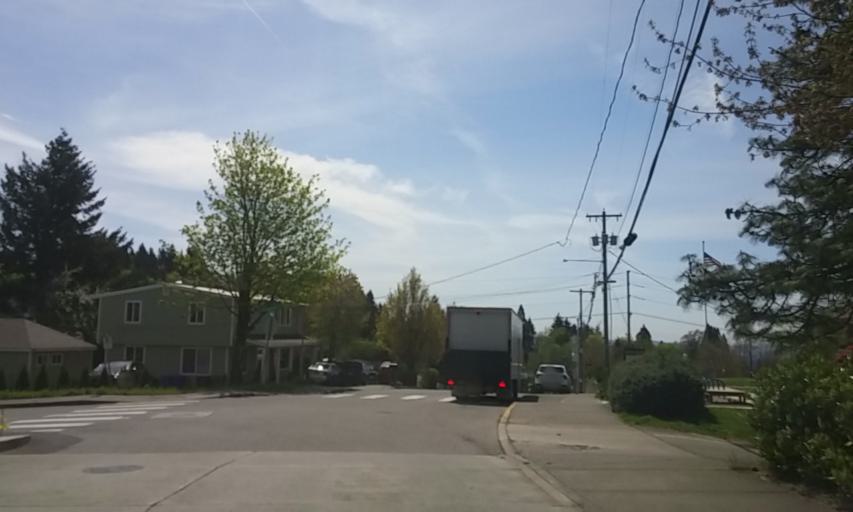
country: US
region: Oregon
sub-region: Washington County
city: West Slope
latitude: 45.5103
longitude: -122.7366
